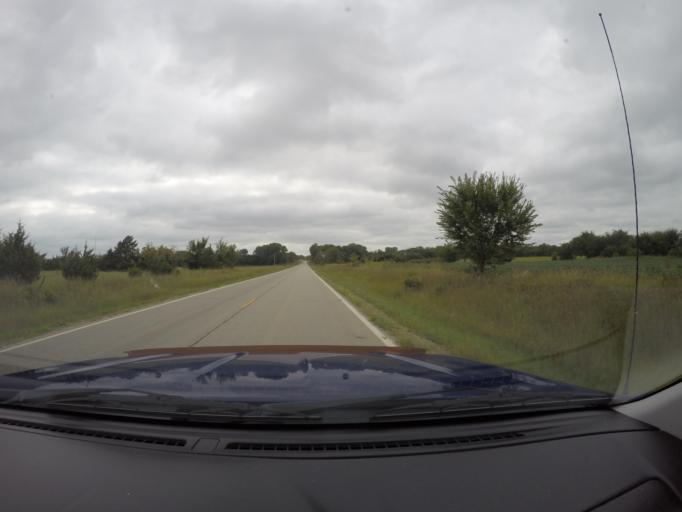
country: US
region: Kansas
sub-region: Geary County
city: Grandview Plaza
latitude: 38.7976
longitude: -96.7132
